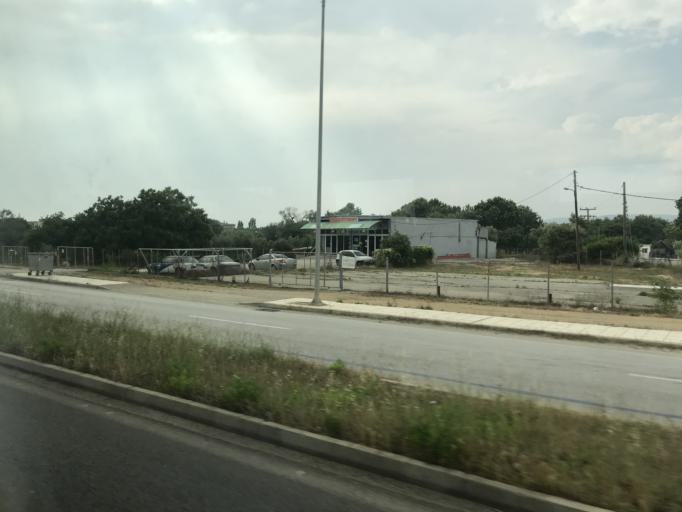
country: GR
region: East Macedonia and Thrace
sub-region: Nomos Evrou
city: Alexandroupoli
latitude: 40.8502
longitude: 25.9025
